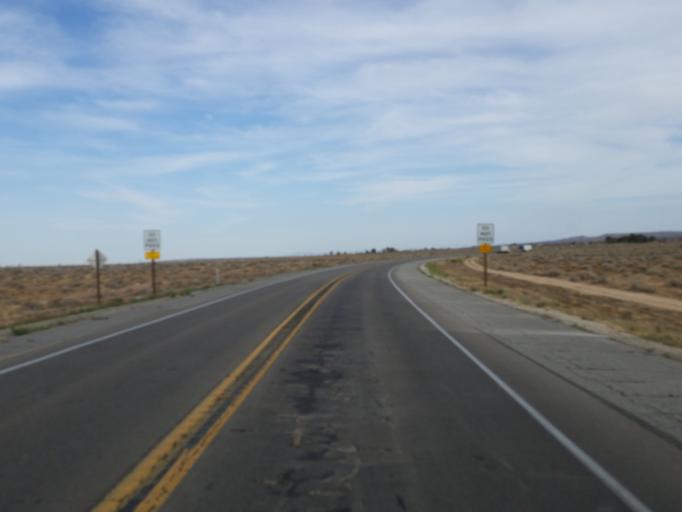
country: US
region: California
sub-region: Kern County
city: Boron
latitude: 35.0090
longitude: -117.6224
